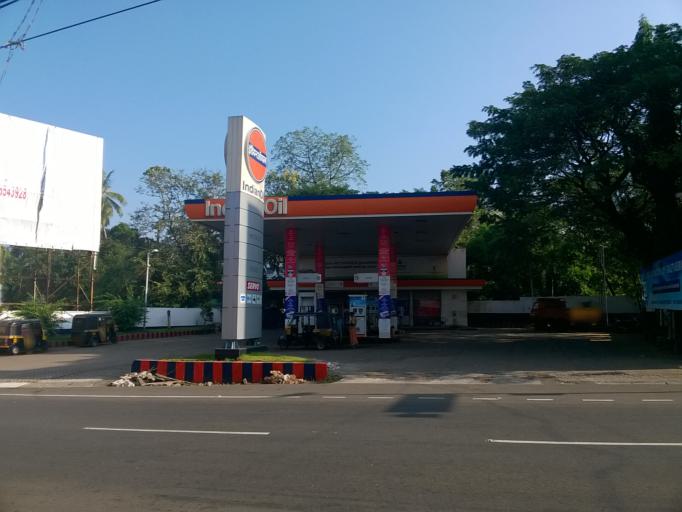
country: IN
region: Kerala
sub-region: Thrissur District
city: Trichur
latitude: 10.5145
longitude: 76.2188
